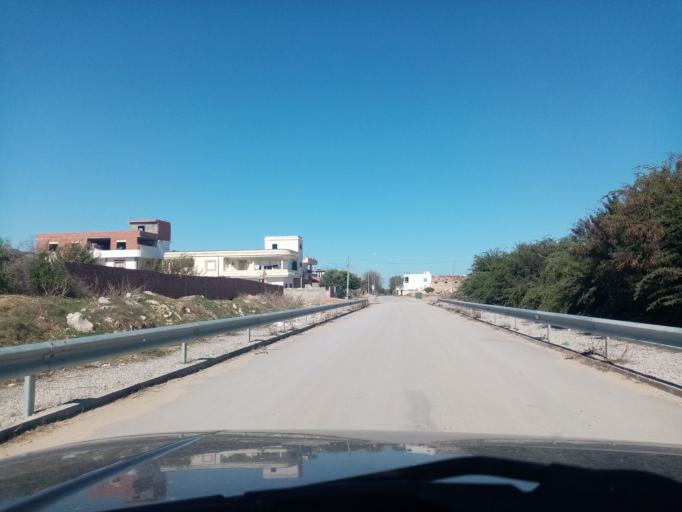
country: TN
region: Nabul
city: Bu `Urqub
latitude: 36.5804
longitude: 10.5697
